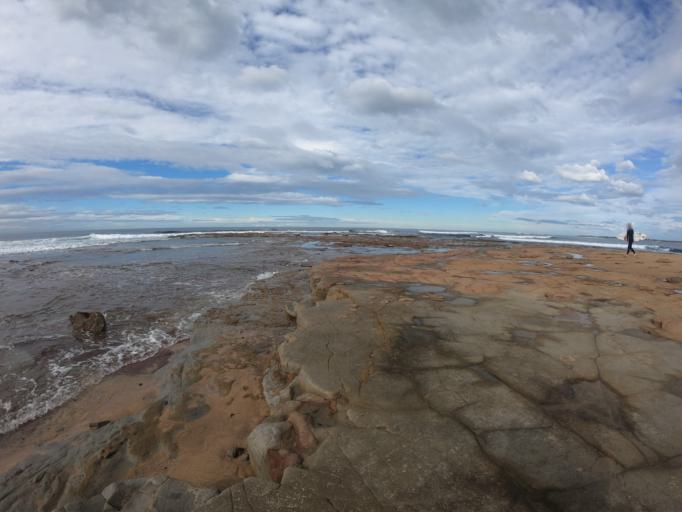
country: AU
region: New South Wales
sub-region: Wollongong
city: Bulli
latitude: -34.3306
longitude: 150.9293
